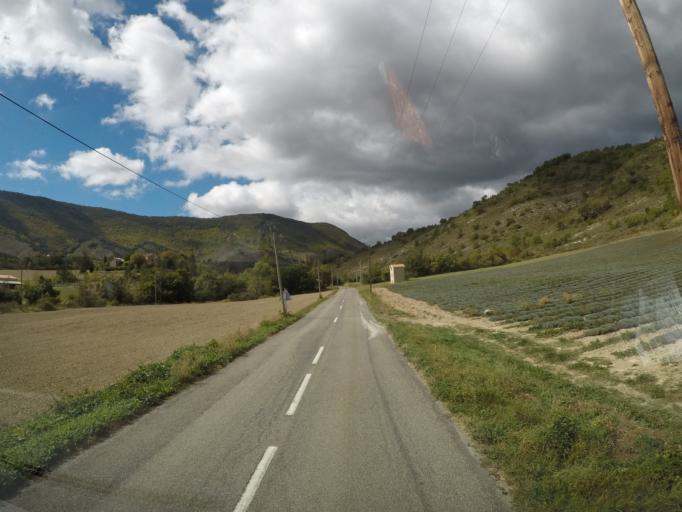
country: FR
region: Provence-Alpes-Cote d'Azur
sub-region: Departement du Vaucluse
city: Sault
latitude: 44.1731
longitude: 5.6037
